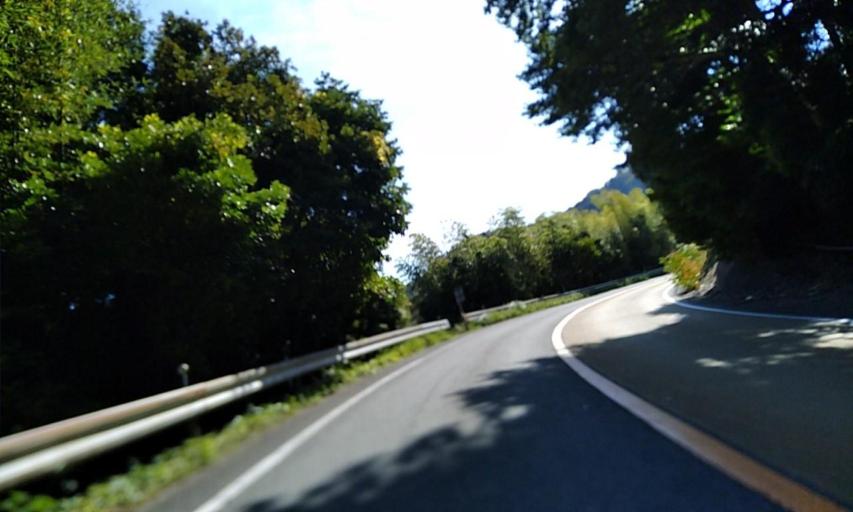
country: JP
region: Wakayama
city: Gobo
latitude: 33.9969
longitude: 135.1927
